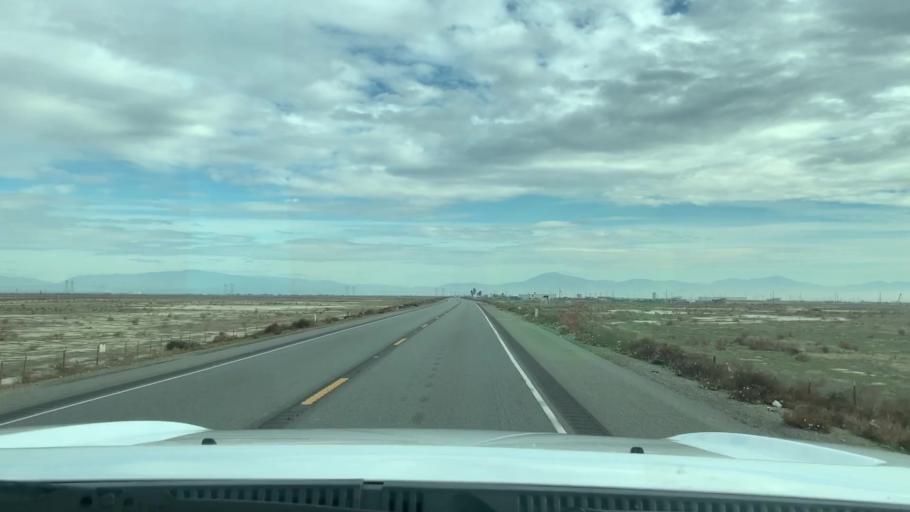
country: US
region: California
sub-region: Kern County
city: Rosedale
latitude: 35.2674
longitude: -119.2725
